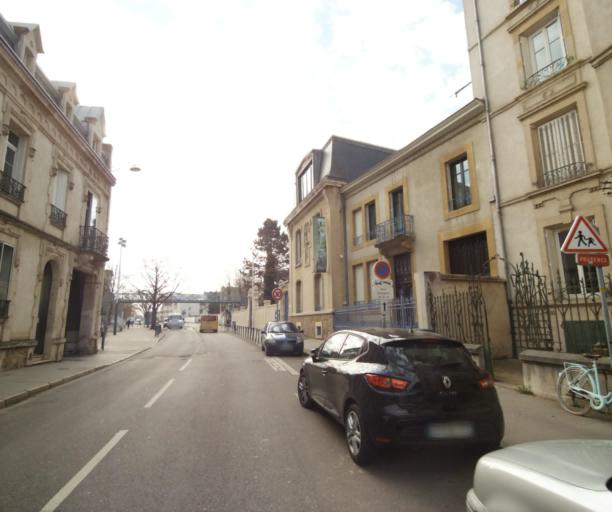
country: FR
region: Lorraine
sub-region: Departement de Meurthe-et-Moselle
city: Villers-les-Nancy
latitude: 48.6808
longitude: 6.1663
